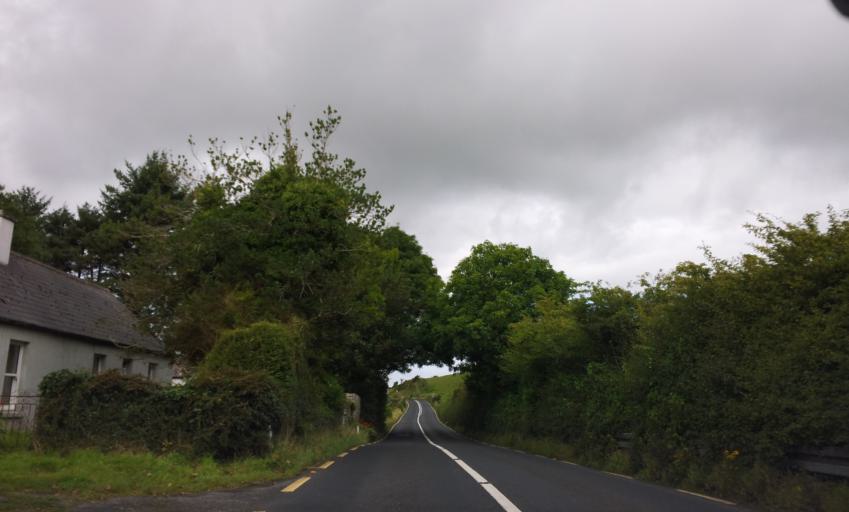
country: IE
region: Munster
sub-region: An Clar
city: Ennis
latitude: 52.9301
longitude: -9.2755
